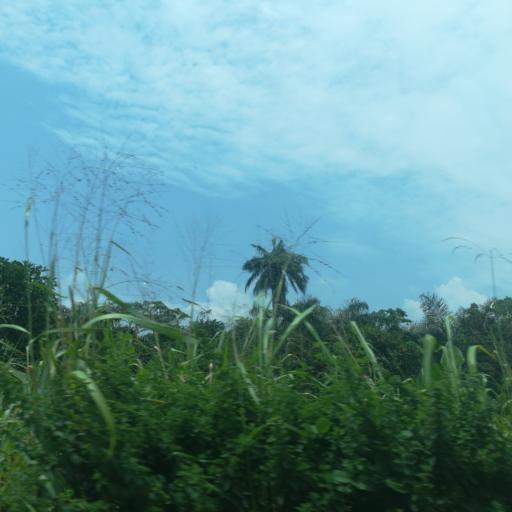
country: NG
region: Lagos
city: Ejirin
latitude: 6.6558
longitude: 3.7992
